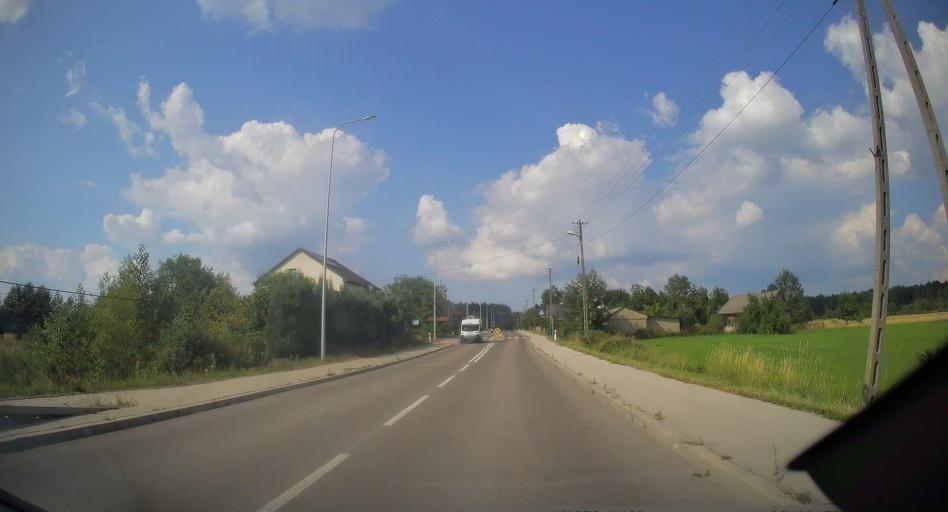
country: PL
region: Swietokrzyskie
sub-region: Powiat konecki
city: Radoszyce
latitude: 51.0128
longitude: 20.2860
